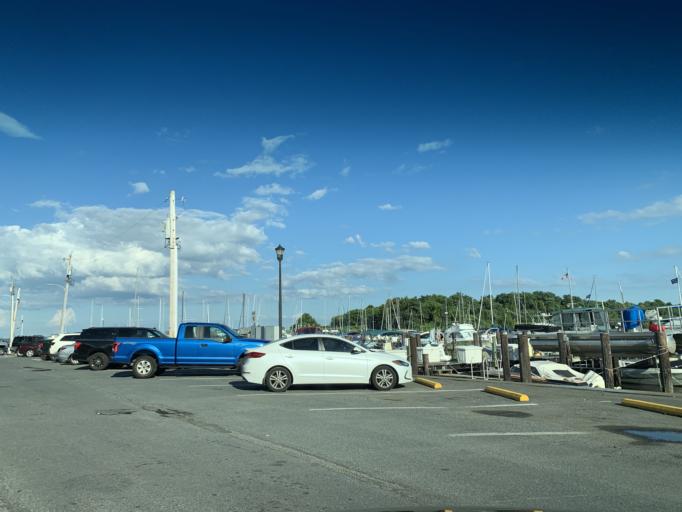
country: US
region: Maryland
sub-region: Harford County
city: Havre de Grace
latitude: 39.5378
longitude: -76.0921
